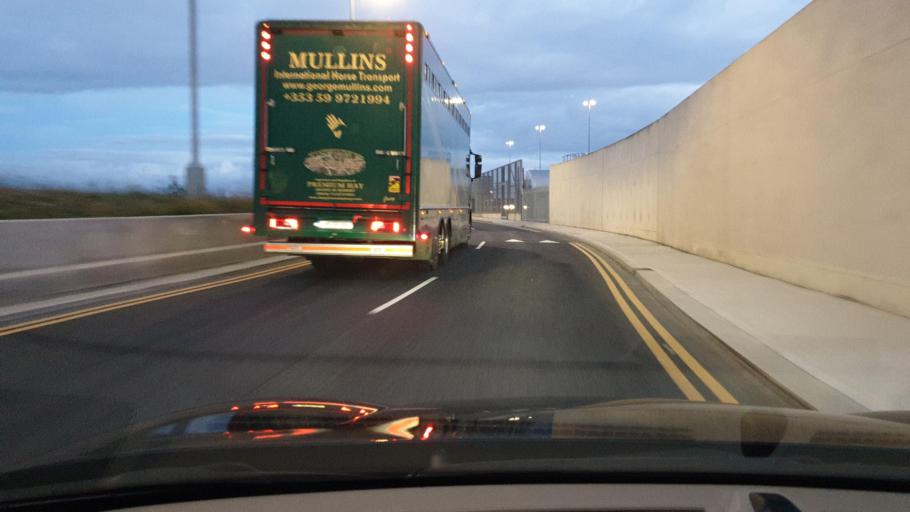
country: IE
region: Leinster
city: Sandymount
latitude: 53.3533
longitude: -6.2074
